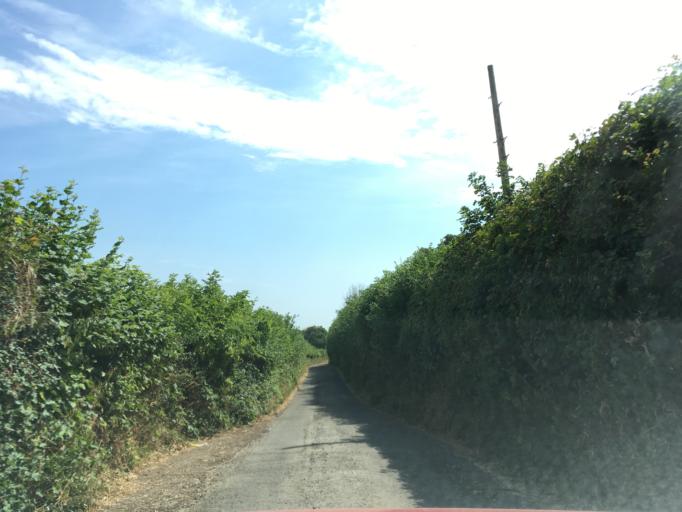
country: GB
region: Wales
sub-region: Monmouthshire
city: Magor
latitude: 51.6009
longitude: -2.8431
